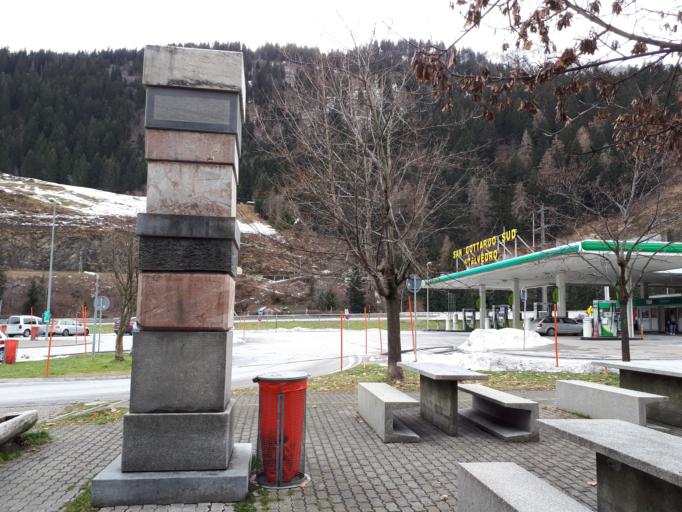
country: CH
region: Ticino
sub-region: Leventina District
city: Airolo
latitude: 46.5212
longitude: 8.6354
